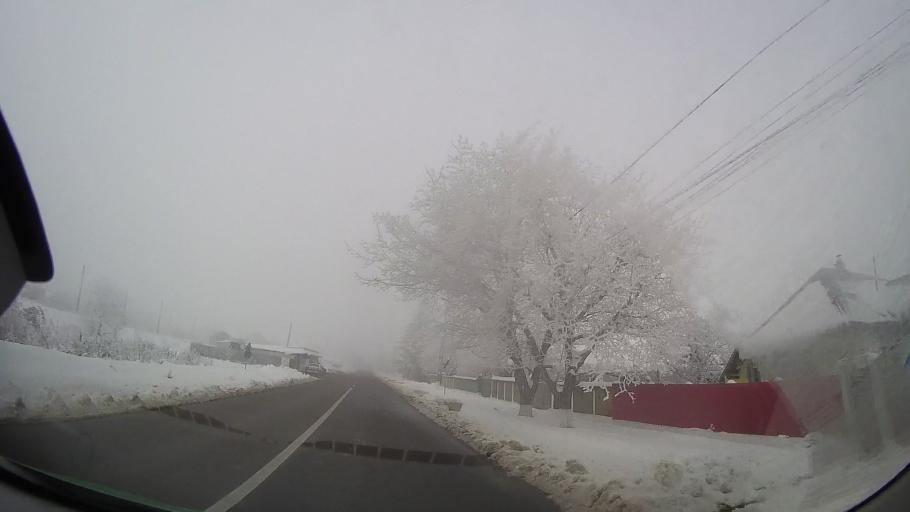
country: RO
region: Iasi
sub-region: Comuna Mircesti
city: Mircesti
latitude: 47.0918
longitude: 26.8217
